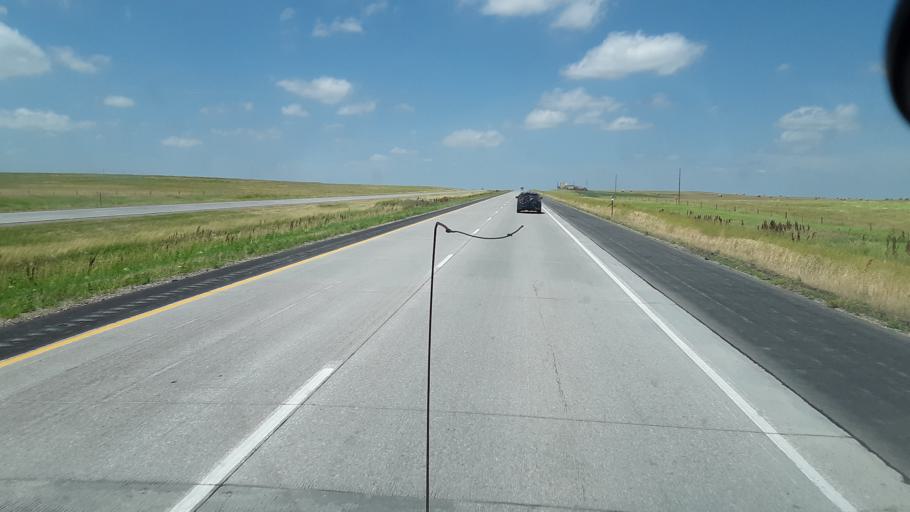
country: US
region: South Dakota
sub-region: Jackson County
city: Kadoka
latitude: 43.8522
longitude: -101.3825
